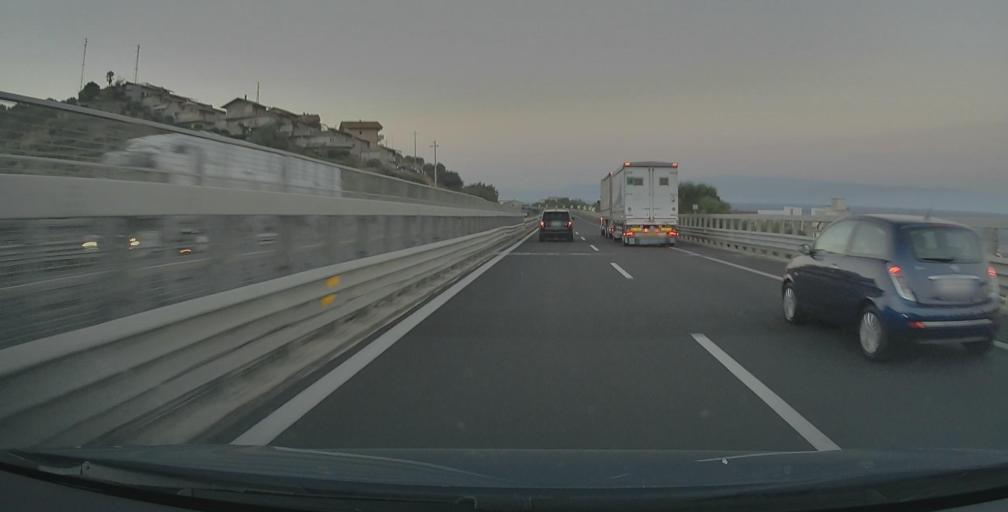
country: IT
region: Sicily
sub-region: Messina
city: Nizza di Sicilia
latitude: 37.9907
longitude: 15.4074
